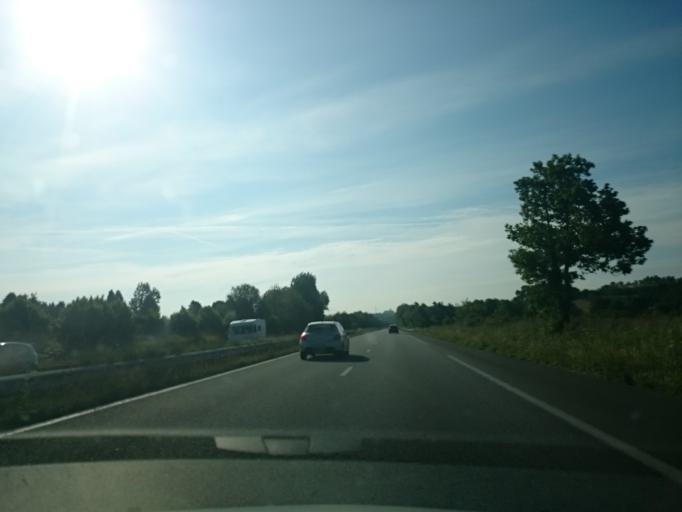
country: FR
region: Brittany
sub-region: Departement du Finistere
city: Saint-Yvi
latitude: 47.9422
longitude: -3.9263
